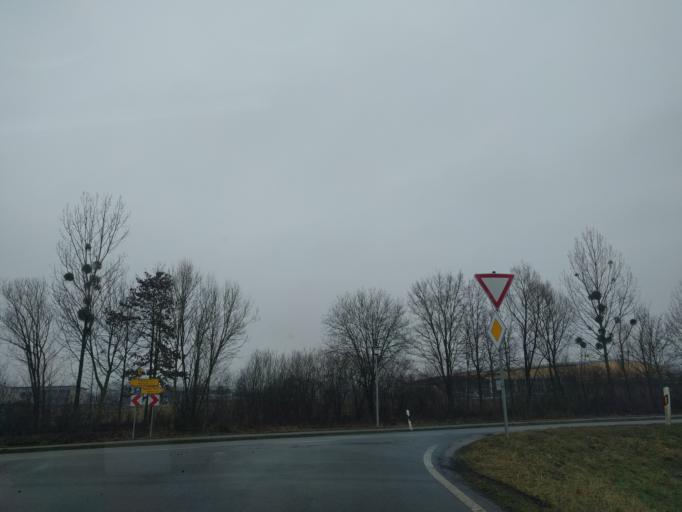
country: DE
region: Bavaria
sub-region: Lower Bavaria
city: Osterhofen
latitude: 48.7124
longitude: 13.0396
